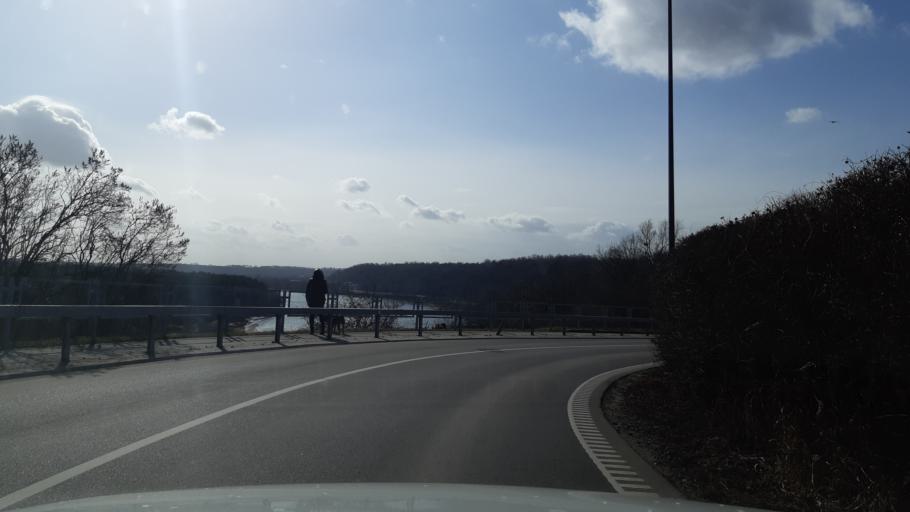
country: LT
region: Kauno apskritis
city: Dainava (Kaunas)
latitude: 54.8938
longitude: 23.9600
